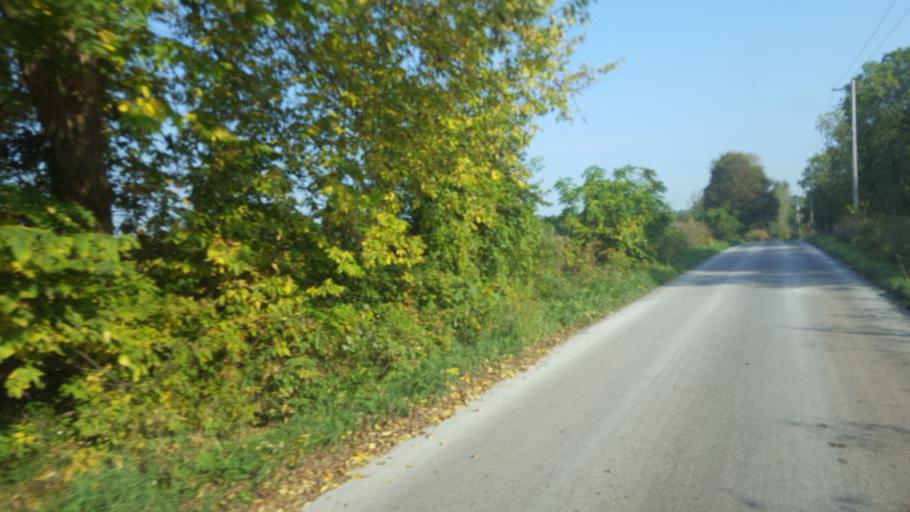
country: US
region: Ohio
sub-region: Knox County
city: Fredericktown
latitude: 40.5385
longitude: -82.6332
